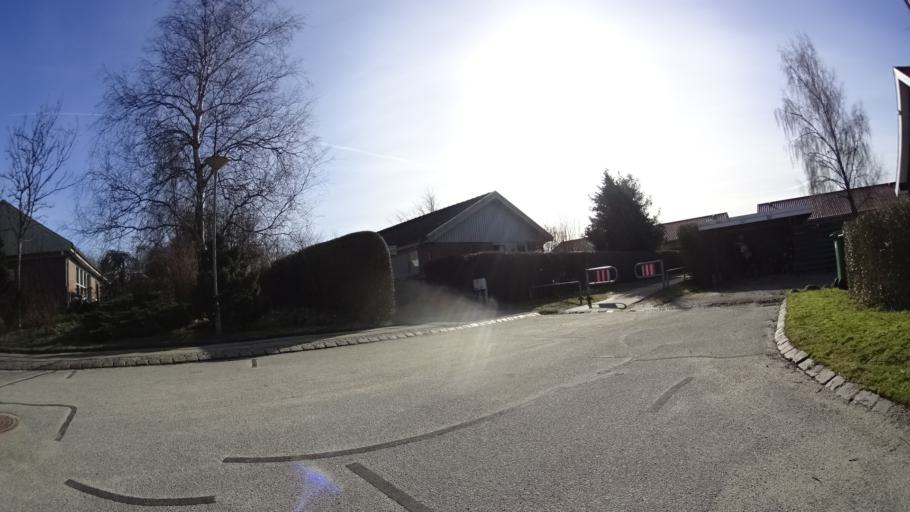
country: DK
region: Central Jutland
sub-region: Arhus Kommune
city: Tranbjerg
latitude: 56.0894
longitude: 10.1153
